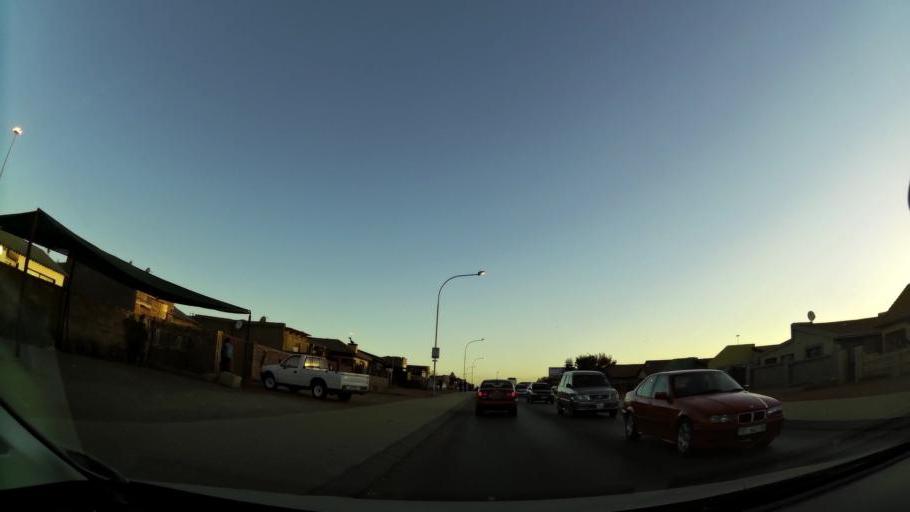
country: ZA
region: Gauteng
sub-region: Ekurhuleni Metropolitan Municipality
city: Tembisa
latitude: -26.0021
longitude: 28.2127
